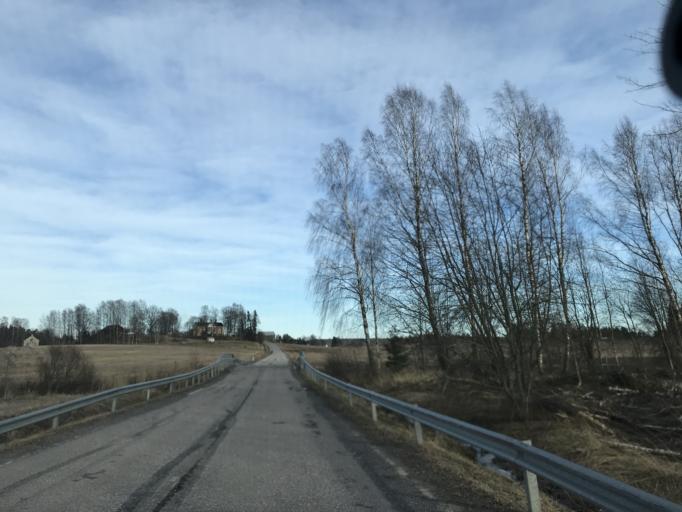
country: FI
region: Uusimaa
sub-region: Raaseporin
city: Pohja
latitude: 60.0900
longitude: 23.4970
